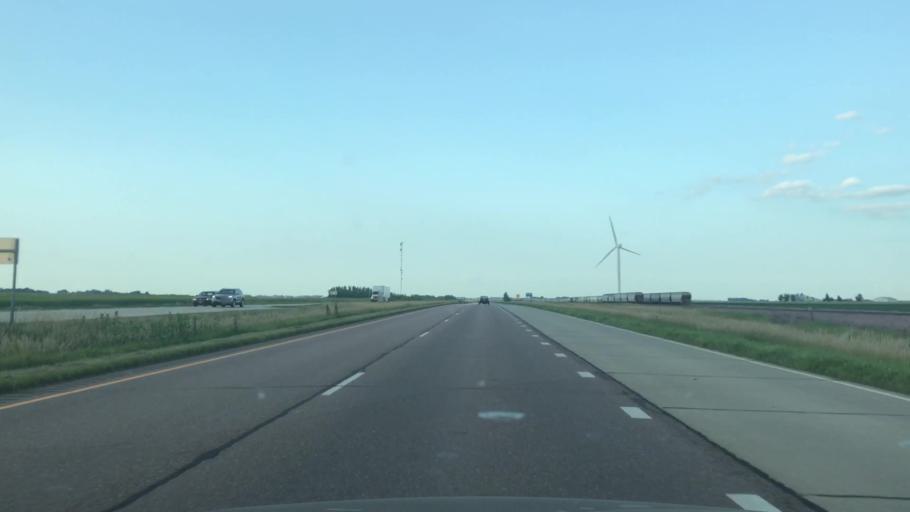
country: US
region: Minnesota
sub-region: Nobles County
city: Worthington
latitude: 43.7124
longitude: -95.4503
